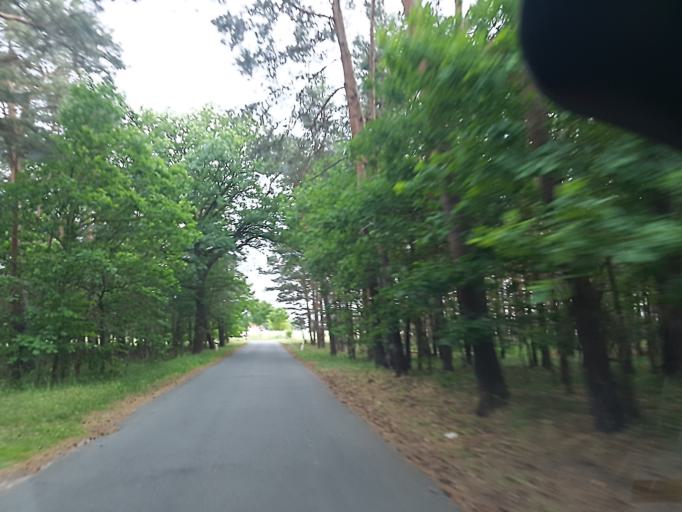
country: DE
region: Saxony-Anhalt
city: Holzdorf
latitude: 51.7673
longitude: 13.1062
